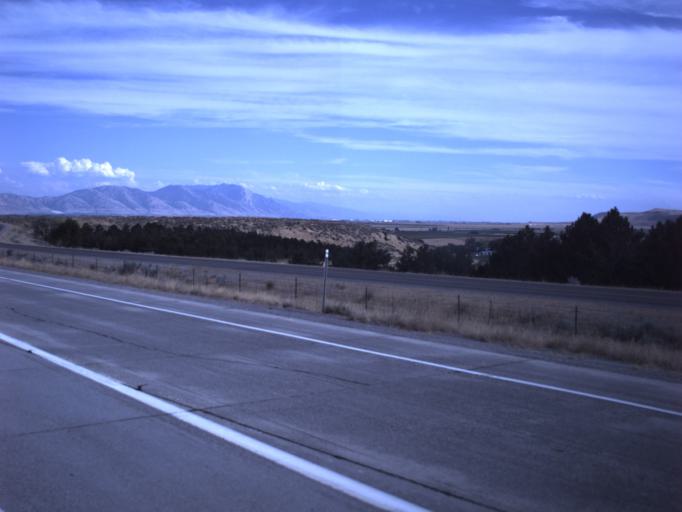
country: US
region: Utah
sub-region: Box Elder County
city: Tremonton
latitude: 41.7222
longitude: -112.2328
